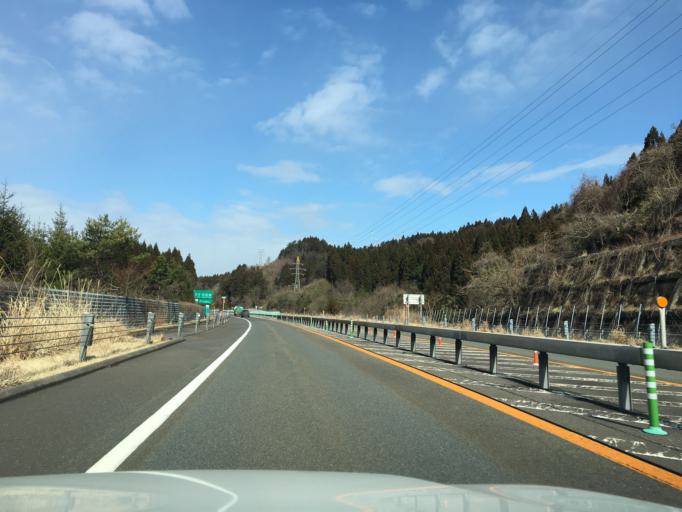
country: JP
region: Akita
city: Akita
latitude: 39.7753
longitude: 140.1193
